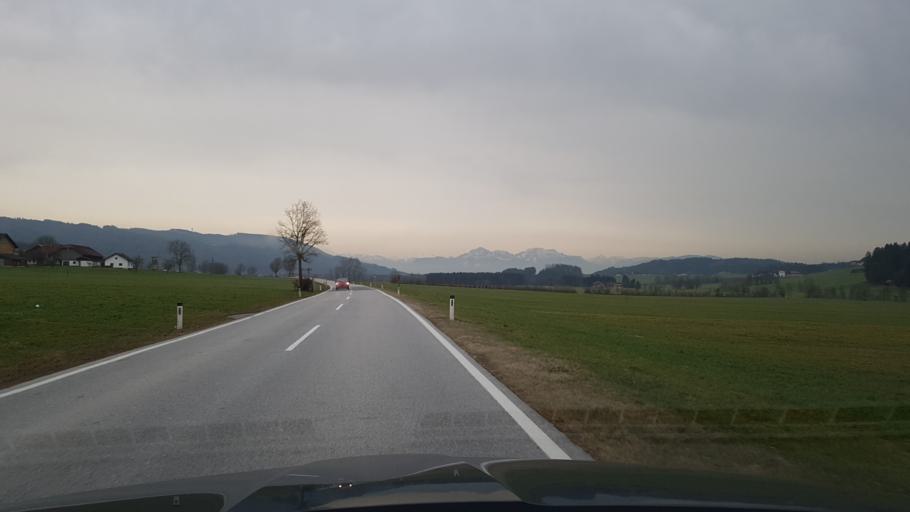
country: AT
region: Salzburg
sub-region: Politischer Bezirk Salzburg-Umgebung
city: Nussdorf am Haunsberg
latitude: 47.9776
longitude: 13.0103
